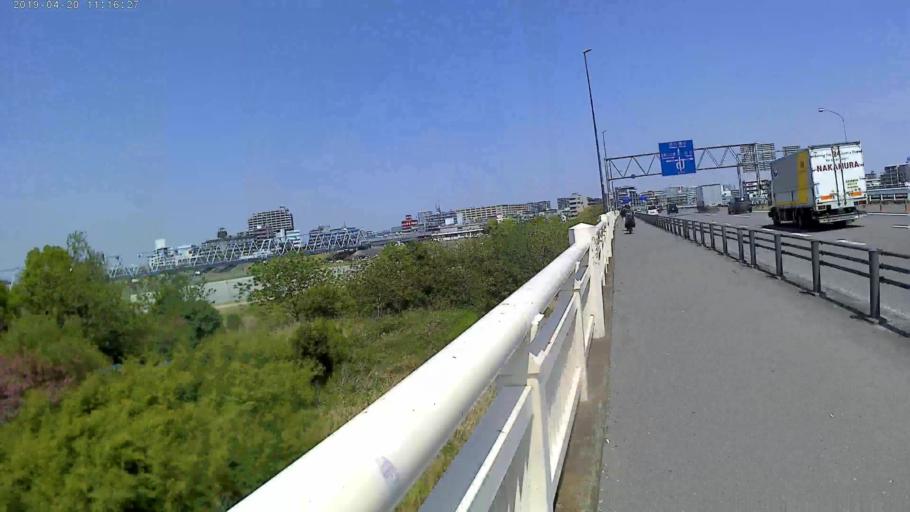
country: JP
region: Kanagawa
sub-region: Kawasaki-shi
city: Kawasaki
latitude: 35.5374
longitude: 139.7084
